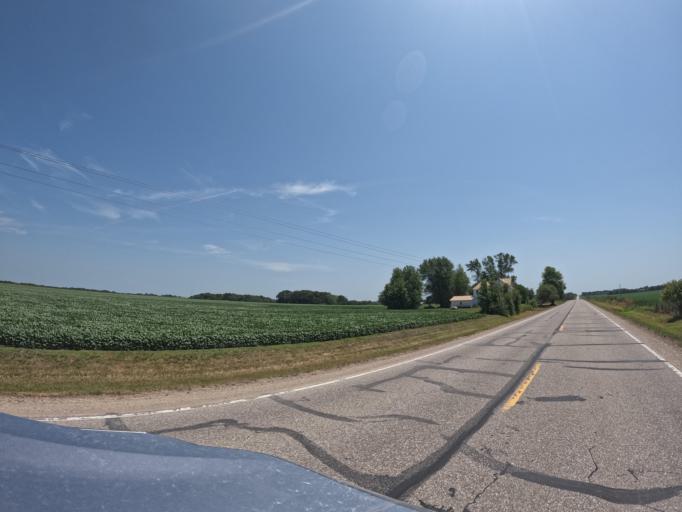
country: US
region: Iowa
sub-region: Henry County
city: Mount Pleasant
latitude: 40.9732
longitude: -91.6124
